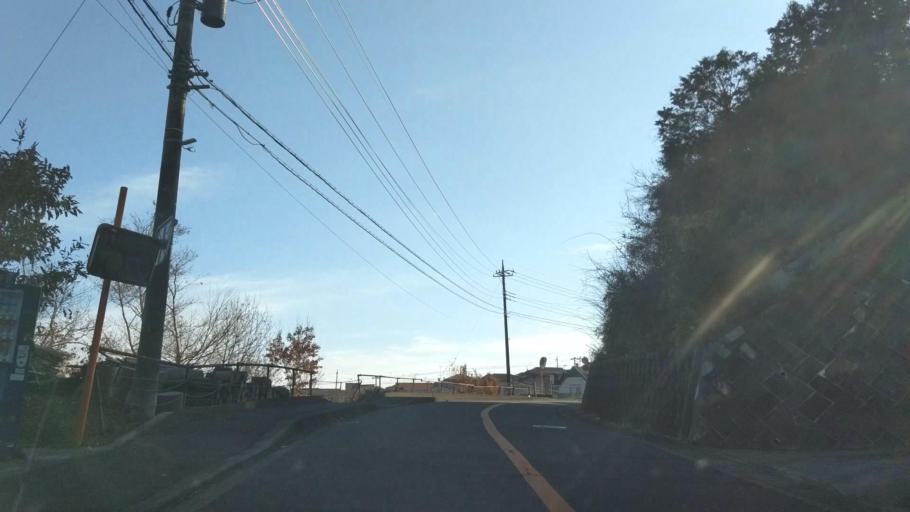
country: JP
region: Kanagawa
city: Hadano
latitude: 35.3683
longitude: 139.2521
